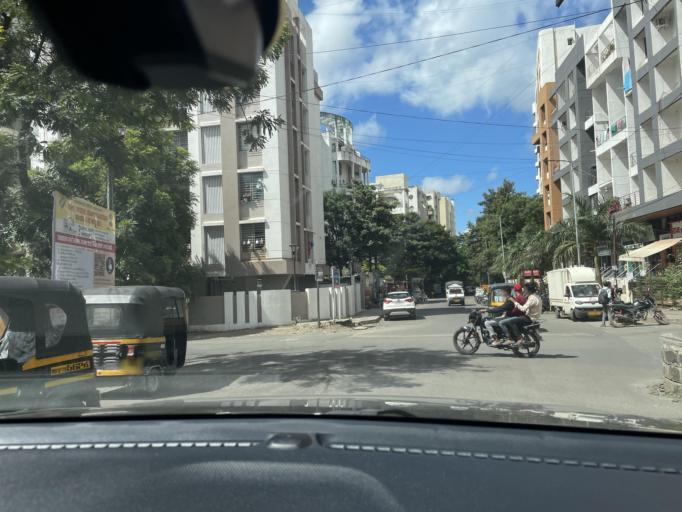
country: IN
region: Maharashtra
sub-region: Pune Division
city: Kharakvasla
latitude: 18.5109
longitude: 73.7771
